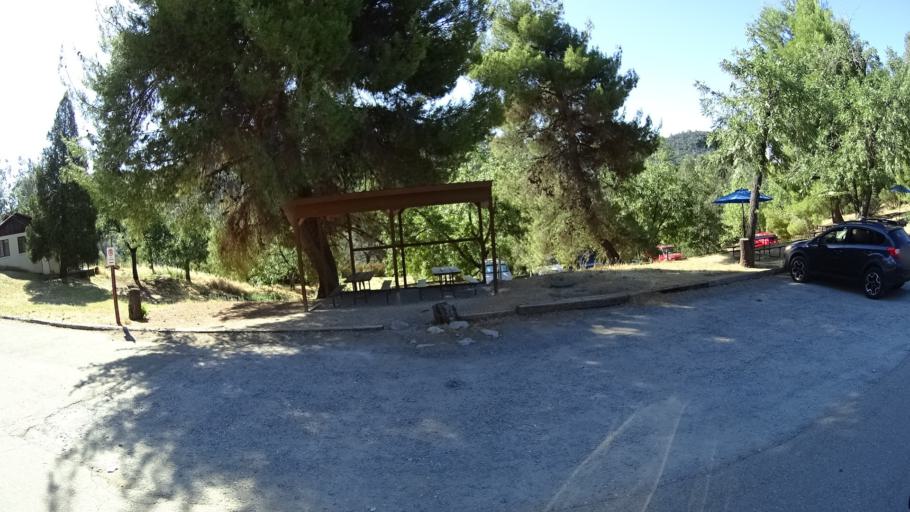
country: US
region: California
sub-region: Calaveras County
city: Murphys
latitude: 38.0689
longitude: -120.4661
